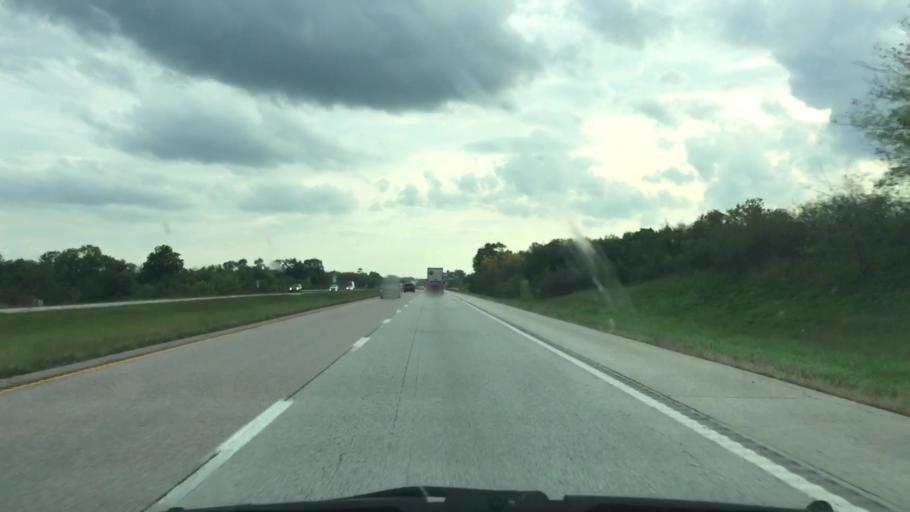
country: US
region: Missouri
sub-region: Clinton County
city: Lathrop
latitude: 39.5643
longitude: -94.2650
